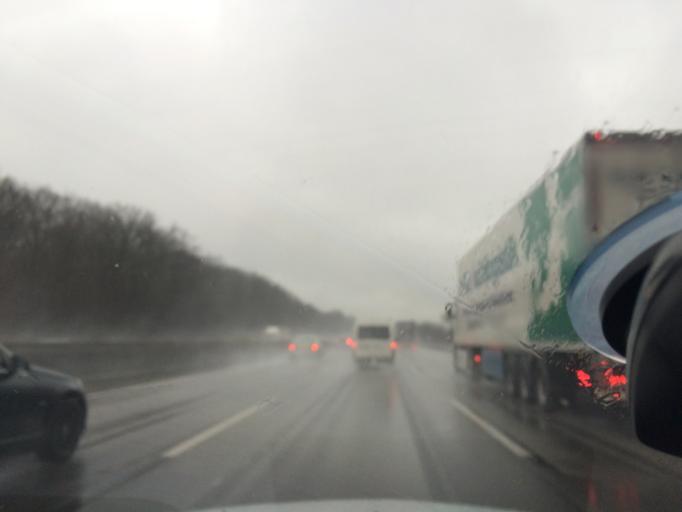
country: DE
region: Hesse
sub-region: Regierungsbezirk Darmstadt
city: Rosbach vor der Hohe
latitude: 50.2948
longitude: 8.6731
